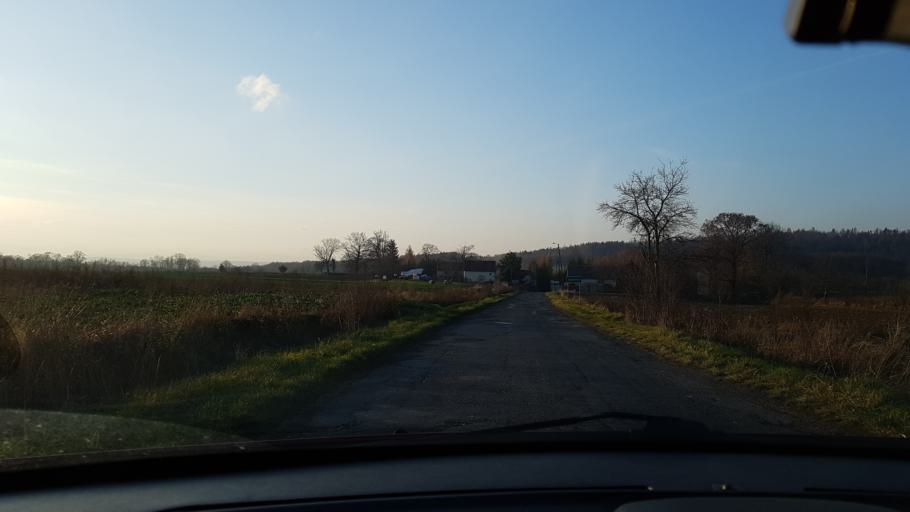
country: PL
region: Lower Silesian Voivodeship
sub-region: Powiat zabkowicki
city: Ziebice
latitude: 50.6571
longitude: 17.0825
